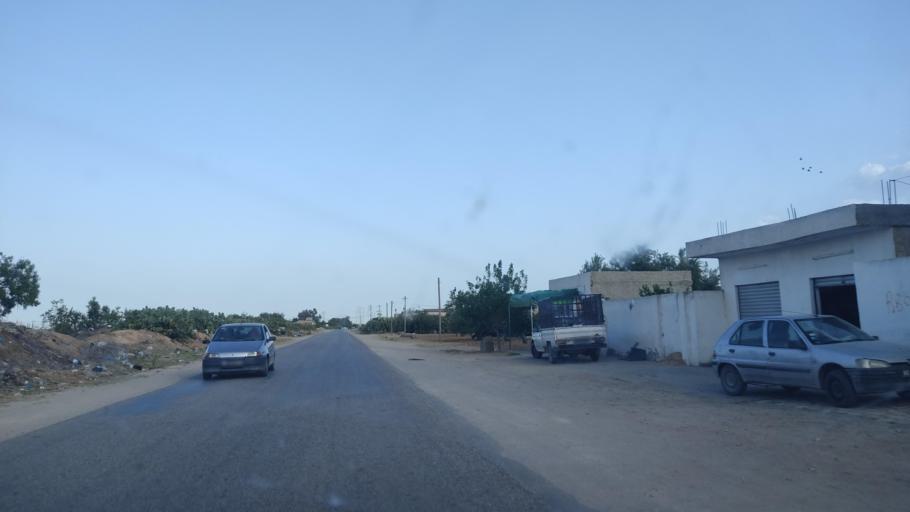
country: TN
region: Safaqis
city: Sfax
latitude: 34.8115
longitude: 10.6613
